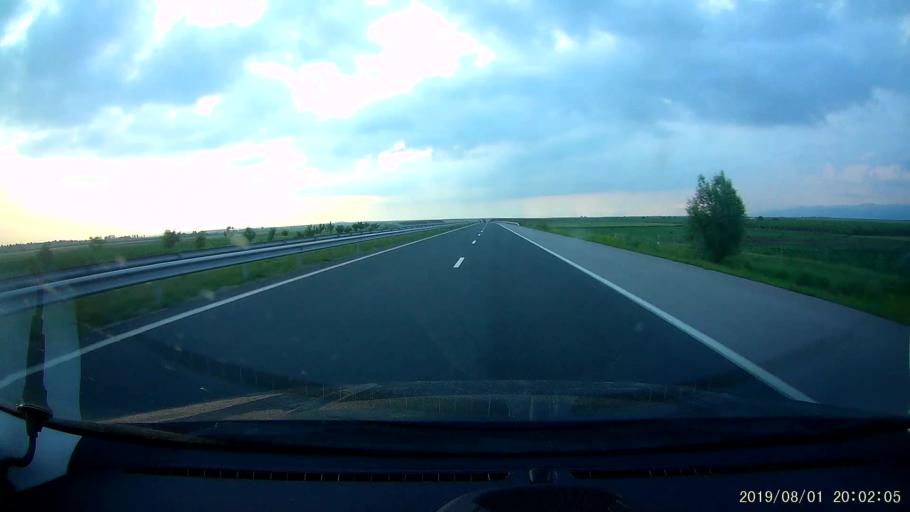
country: BG
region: Yambol
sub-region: Obshtina Straldzha
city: Straldzha
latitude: 42.5582
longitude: 26.6420
